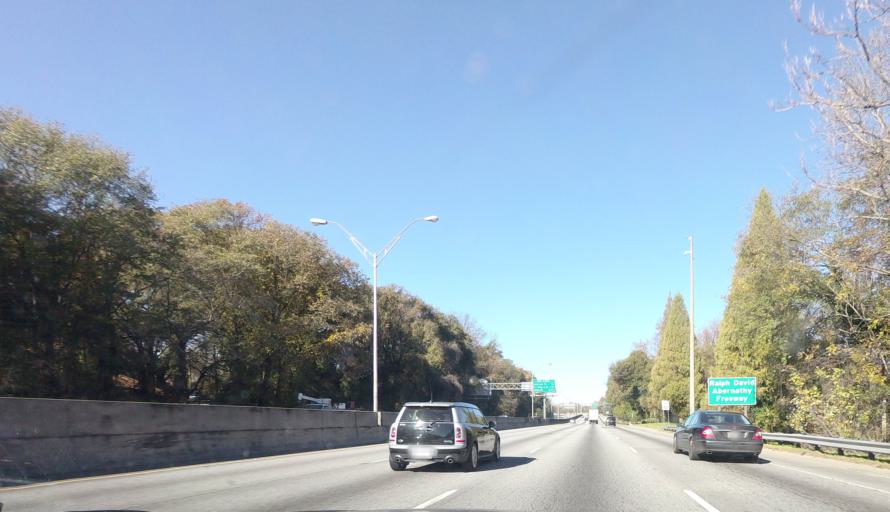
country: US
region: Georgia
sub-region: Fulton County
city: Atlanta
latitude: 33.7439
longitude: -84.4247
